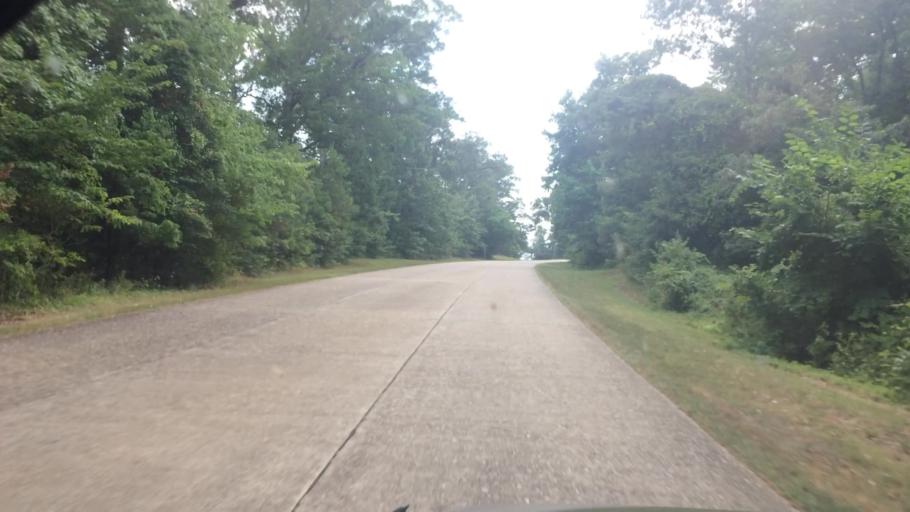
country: US
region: Virginia
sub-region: City of Williamsburg
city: Williamsburg
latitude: 37.2188
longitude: -76.7007
